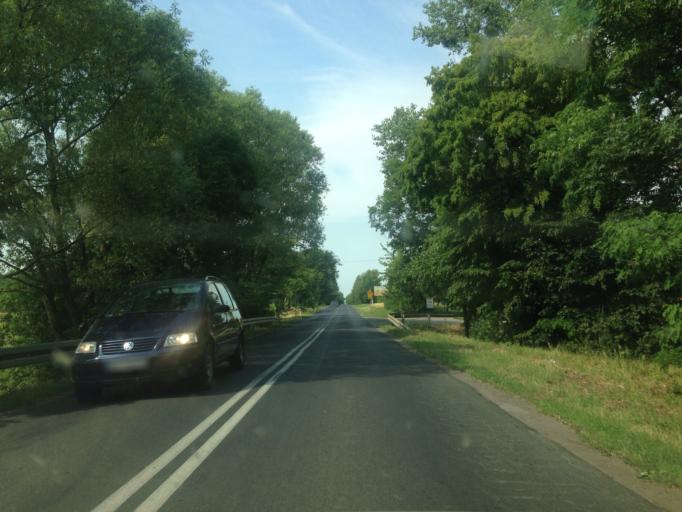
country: PL
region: Kujawsko-Pomorskie
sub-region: Powiat brodnicki
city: Bobrowo
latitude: 53.2756
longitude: 19.3152
